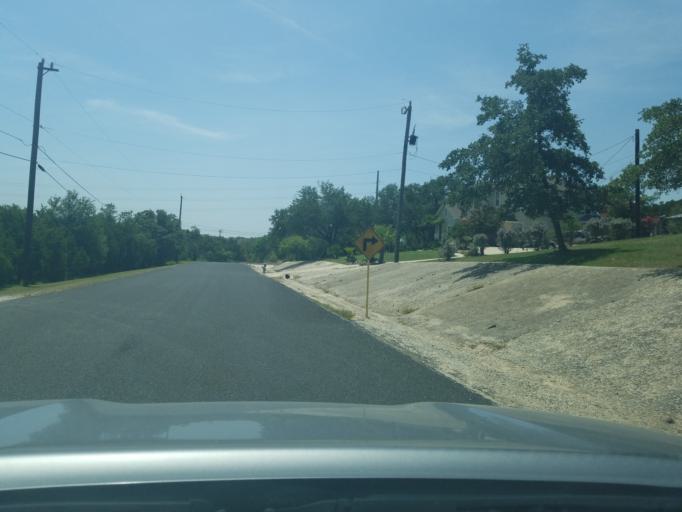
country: US
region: Texas
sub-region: Bexar County
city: Timberwood Park
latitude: 29.6720
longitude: -98.5069
